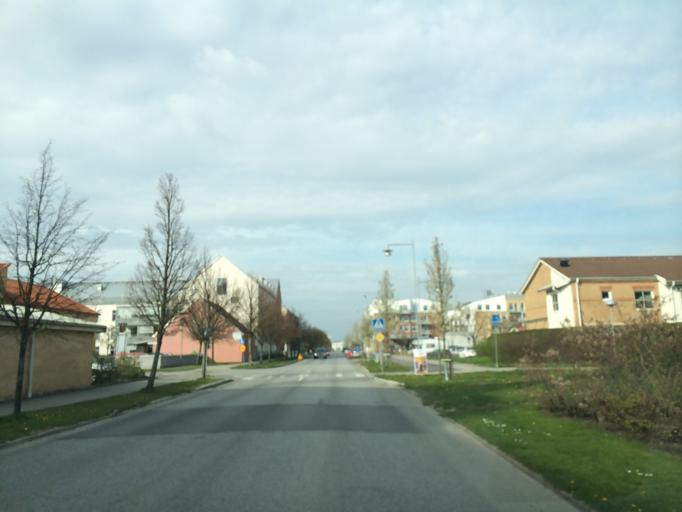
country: SE
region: Skane
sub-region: Lomma Kommun
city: Lomma
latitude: 55.6712
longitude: 13.0669
